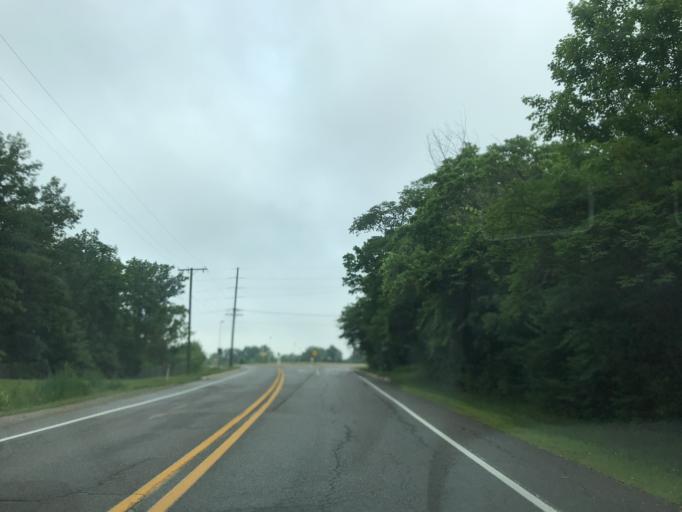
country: US
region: Michigan
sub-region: Washtenaw County
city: Ypsilanti
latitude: 42.2733
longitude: -83.6376
